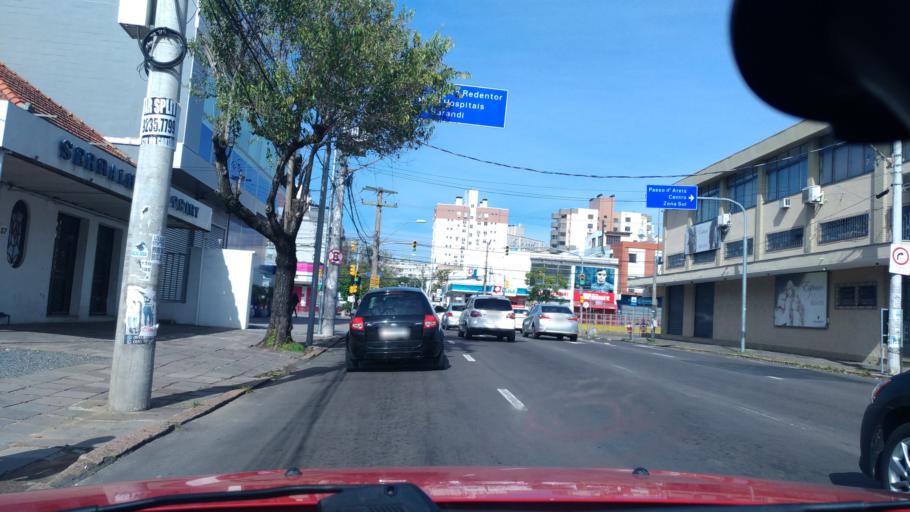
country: BR
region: Rio Grande do Sul
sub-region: Porto Alegre
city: Porto Alegre
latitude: -30.0111
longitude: -51.1662
